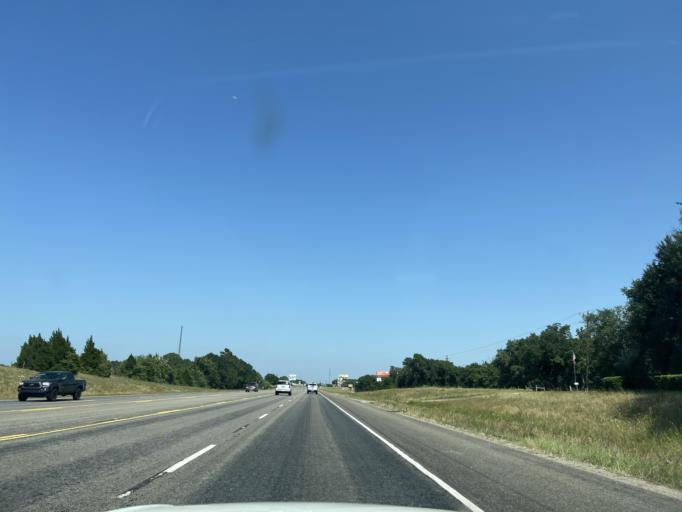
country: US
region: Texas
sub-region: Washington County
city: Brenham
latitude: 30.1709
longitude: -96.4451
